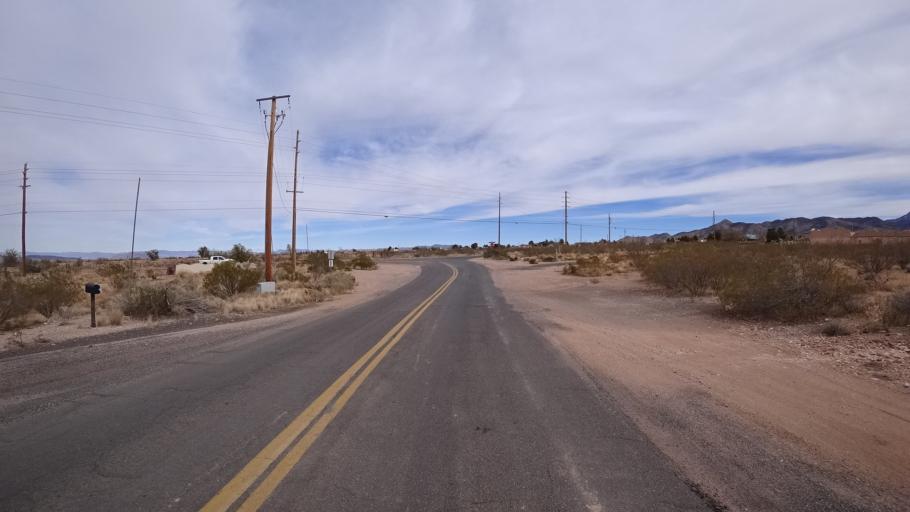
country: US
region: Arizona
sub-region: Mohave County
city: Kingman
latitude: 35.1807
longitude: -113.9979
